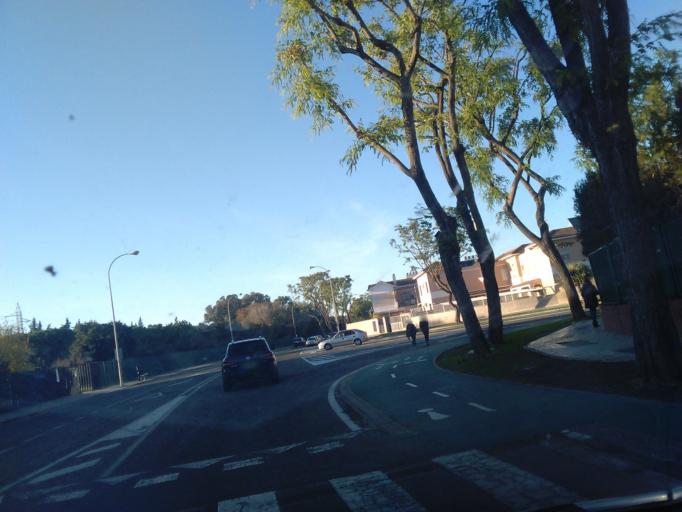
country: ES
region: Andalusia
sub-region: Provincia de Sevilla
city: Sevilla
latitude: 37.3918
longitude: -5.9257
